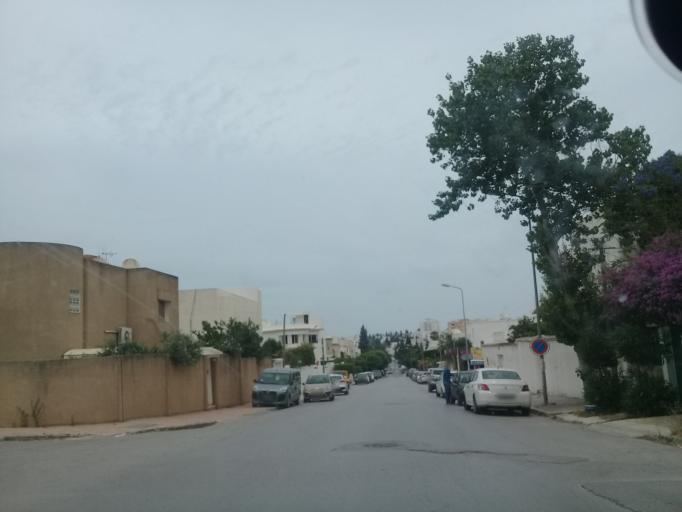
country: TN
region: Tunis
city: Tunis
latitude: 36.8437
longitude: 10.1553
